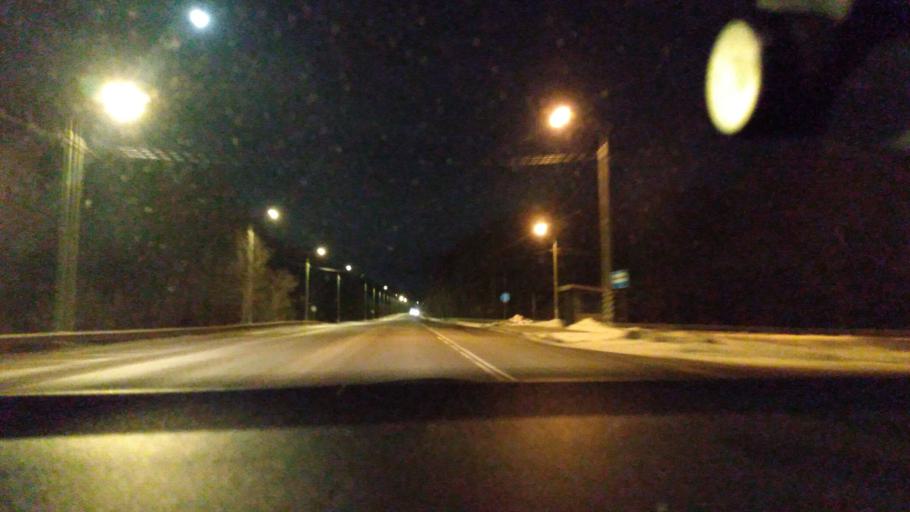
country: RU
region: Moskovskaya
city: Il'inskiy Pogost
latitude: 55.4777
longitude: 38.9440
